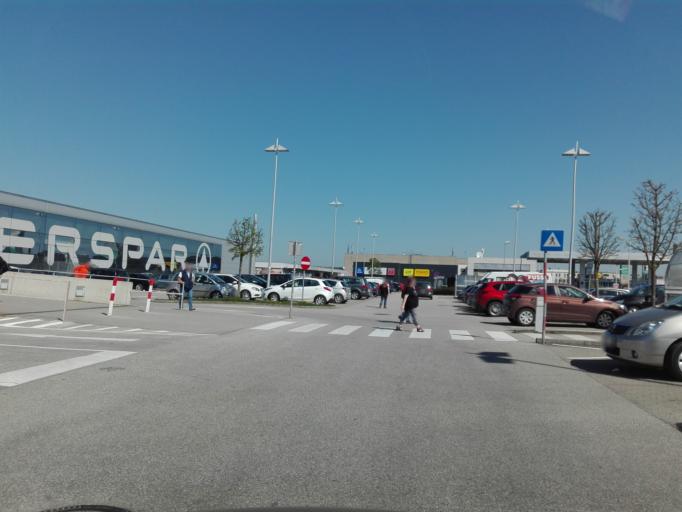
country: AT
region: Upper Austria
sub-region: Steyr Stadt
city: Steyr
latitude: 48.0527
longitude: 14.4201
